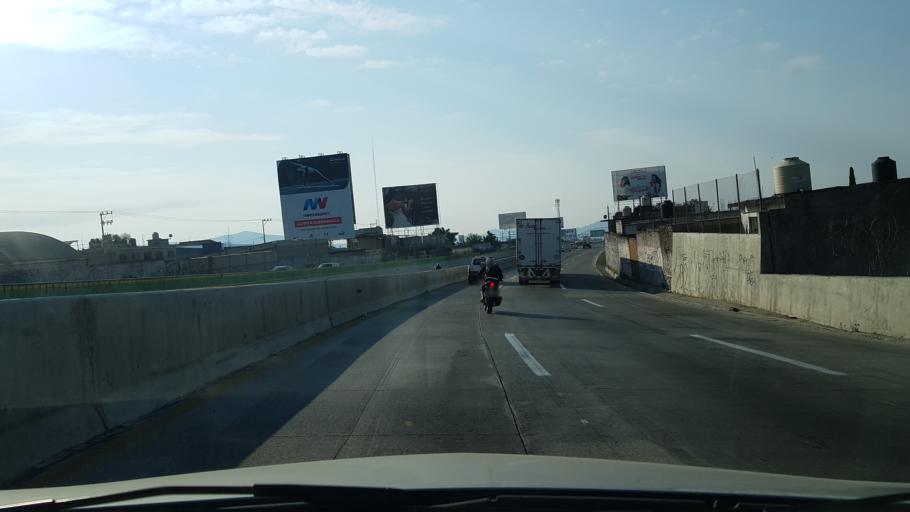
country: MX
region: Morelos
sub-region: Cuernavaca
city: Colonia los Cerritos
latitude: 18.9530
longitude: -99.1921
